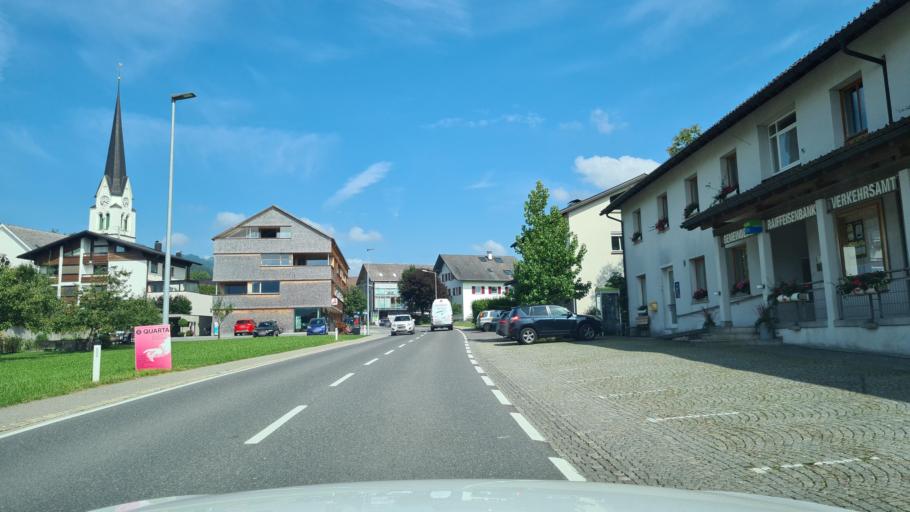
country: AT
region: Vorarlberg
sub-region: Politischer Bezirk Bregenz
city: Egg
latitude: 47.4496
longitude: 9.9181
